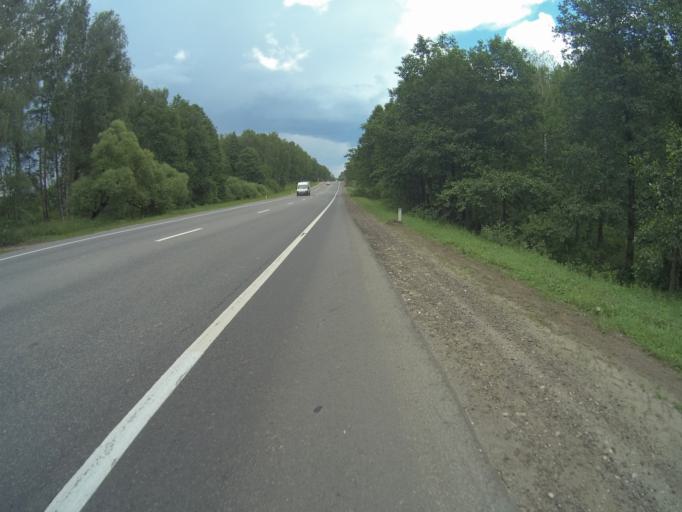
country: RU
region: Vladimir
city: Orgtrud
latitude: 56.2097
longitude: 40.6440
